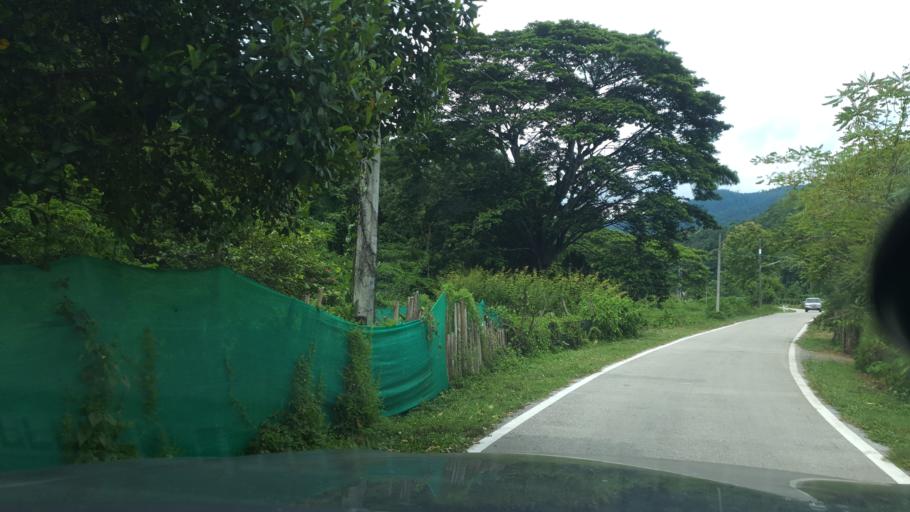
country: TH
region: Lampang
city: Hang Chat
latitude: 18.4285
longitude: 99.2669
